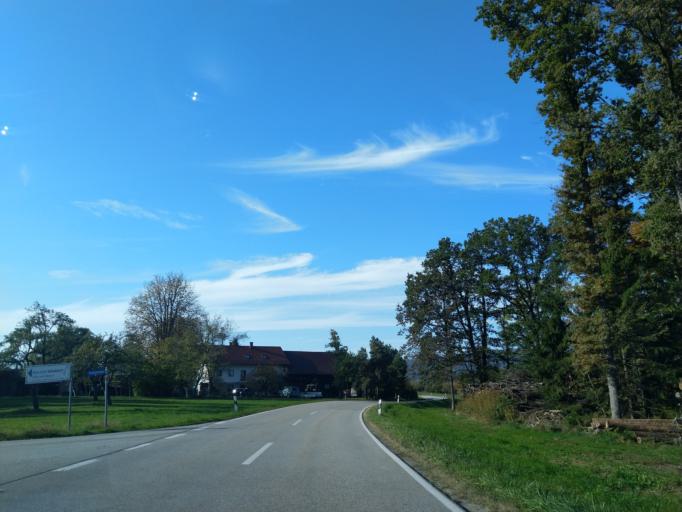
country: DE
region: Bavaria
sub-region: Lower Bavaria
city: Bernried
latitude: 48.8911
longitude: 12.9082
